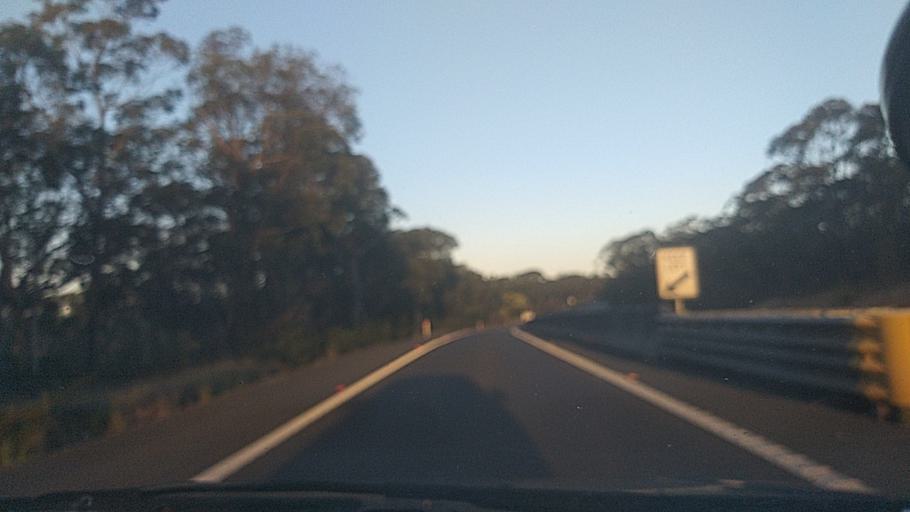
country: AU
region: New South Wales
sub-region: Wollongong
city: Mount Keira
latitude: -34.3215
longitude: 150.7625
